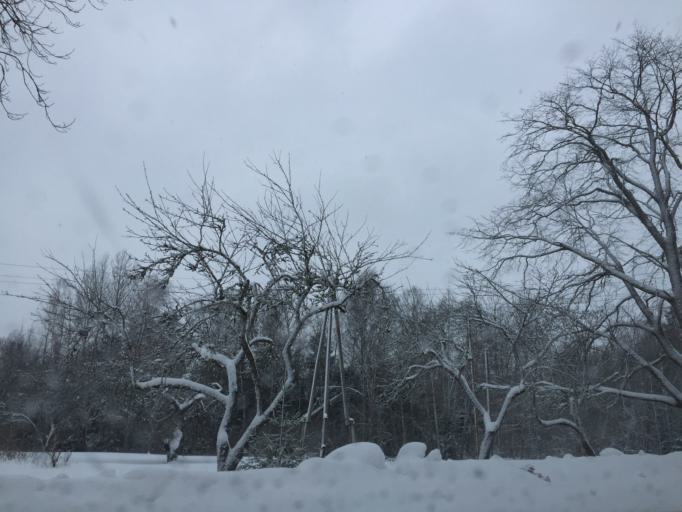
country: LV
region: Amatas Novads
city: Drabesi
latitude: 57.1674
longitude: 25.2773
